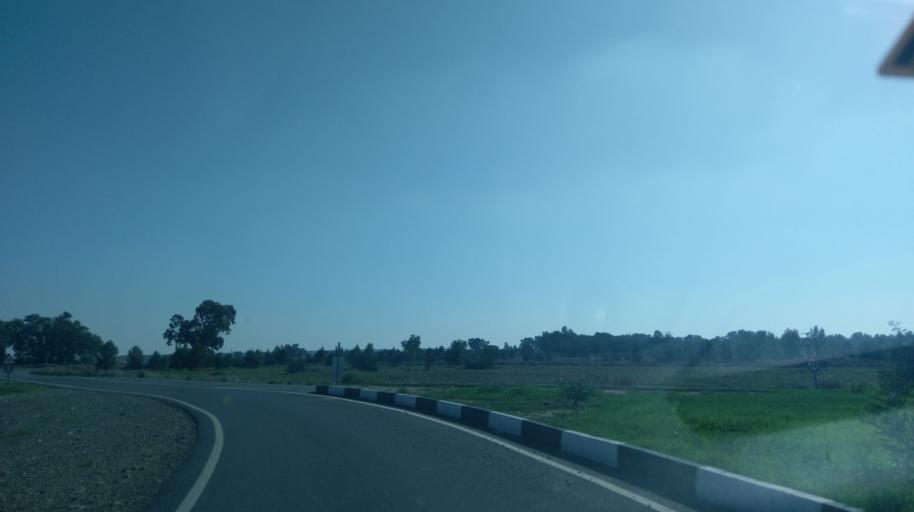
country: CY
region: Larnaka
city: Athienou
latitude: 35.1432
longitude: 33.5157
